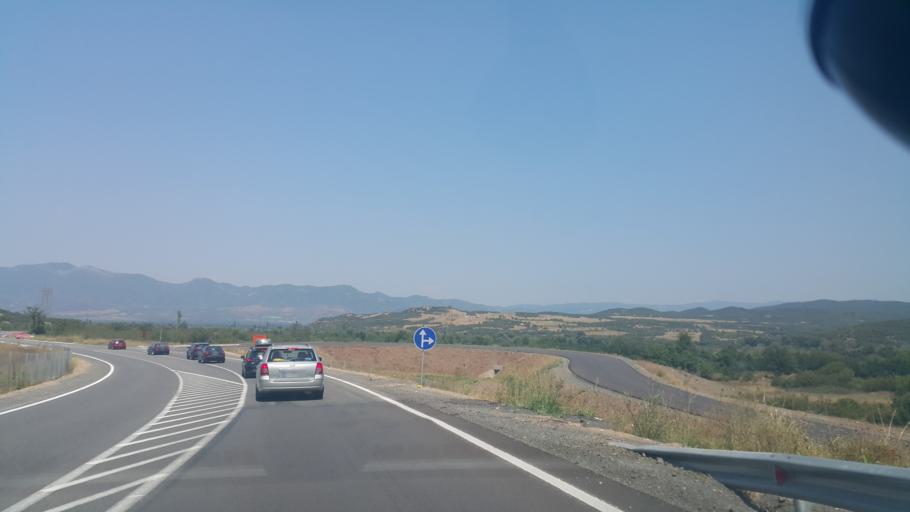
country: MK
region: Gevgelija
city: Miravci
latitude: 41.2642
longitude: 22.4753
